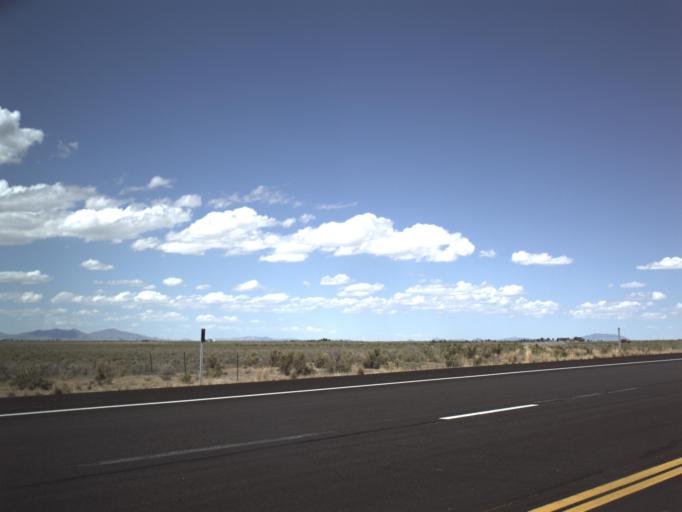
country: US
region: Utah
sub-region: Millard County
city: Delta
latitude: 39.3478
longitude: -112.4958
